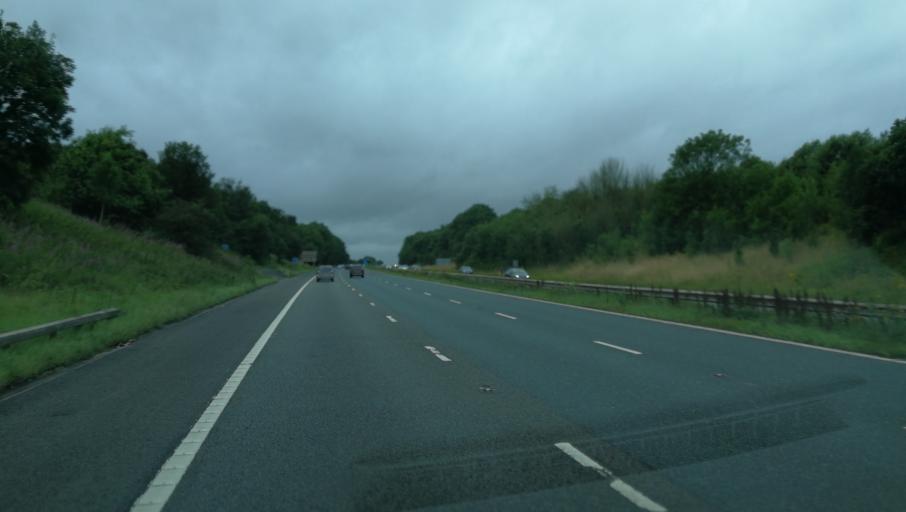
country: GB
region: England
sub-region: Borough of Wigan
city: Atherton
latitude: 53.5499
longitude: -2.4738
